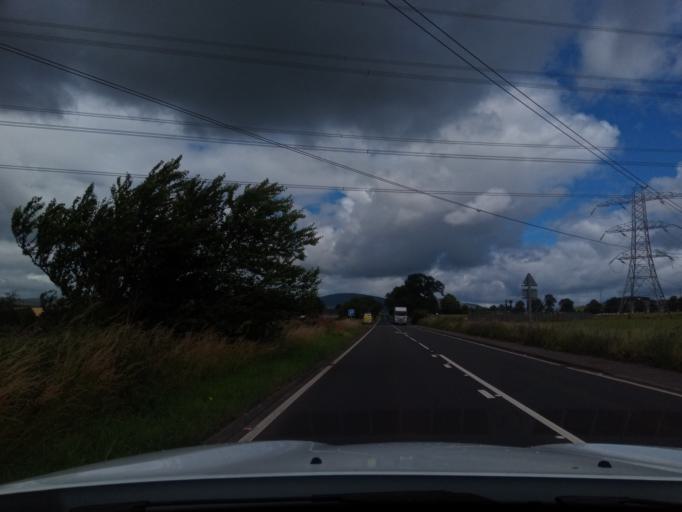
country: GB
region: Scotland
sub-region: Fife
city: Kincardine
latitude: 56.0878
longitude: -3.7193
